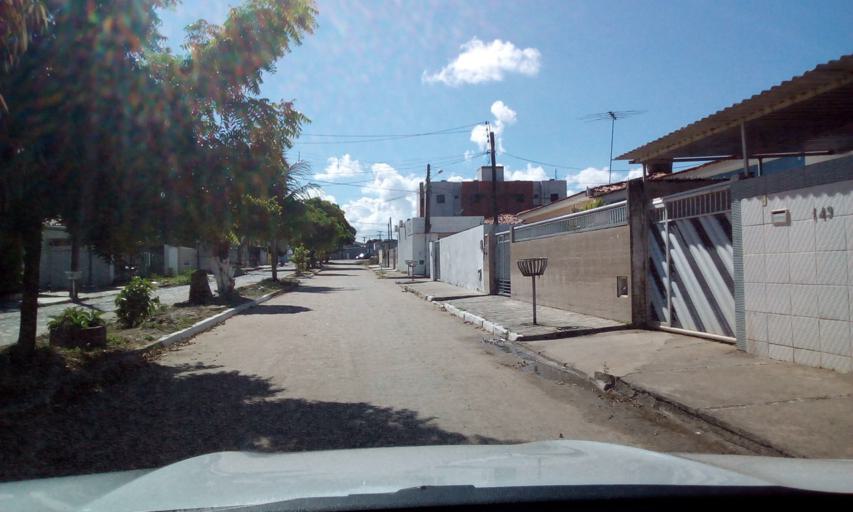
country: BR
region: Paraiba
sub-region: Joao Pessoa
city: Joao Pessoa
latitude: -7.1812
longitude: -34.8588
